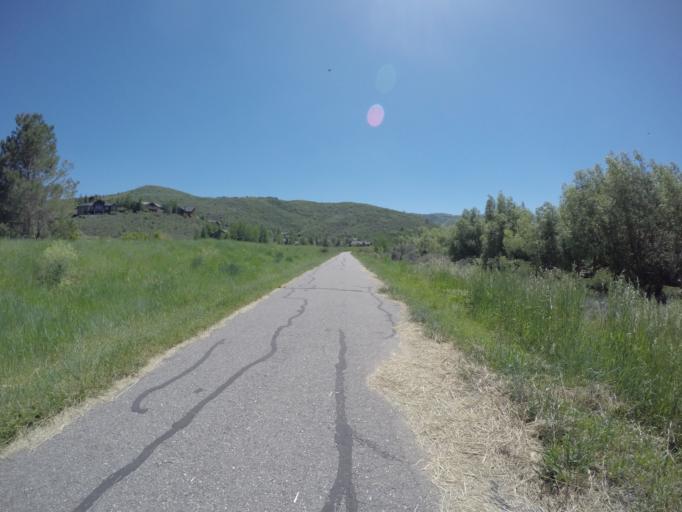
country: US
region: Utah
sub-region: Summit County
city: Park City
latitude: 40.6655
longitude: -111.4866
